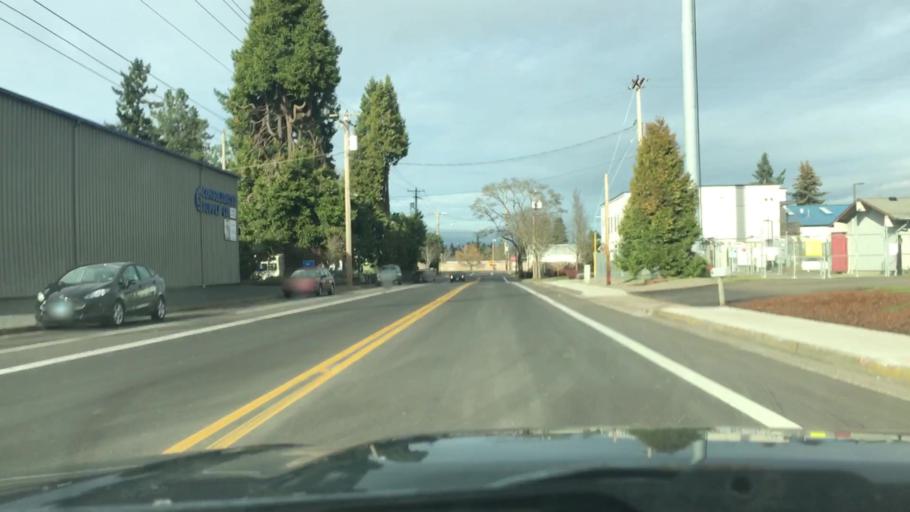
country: US
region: Oregon
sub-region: Lane County
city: Eugene
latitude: 44.0615
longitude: -123.1226
